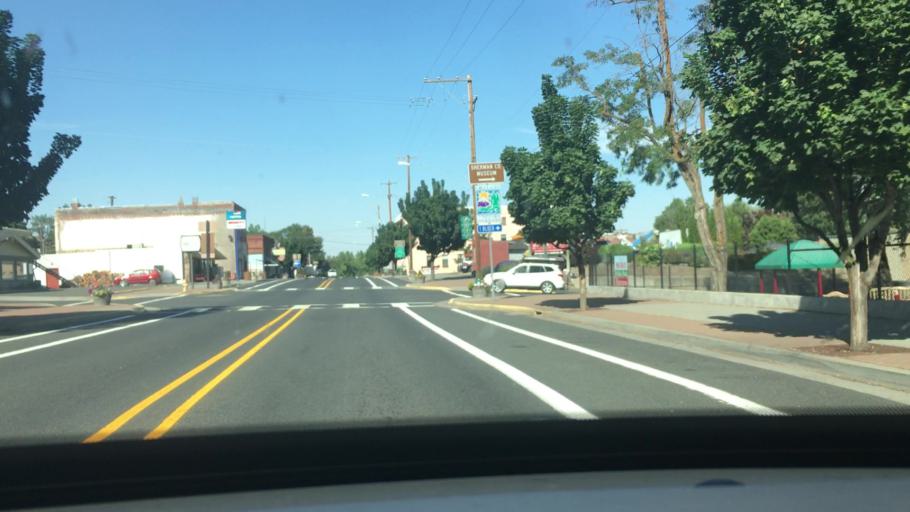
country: US
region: Oregon
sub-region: Sherman County
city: Moro
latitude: 45.4833
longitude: -120.7319
